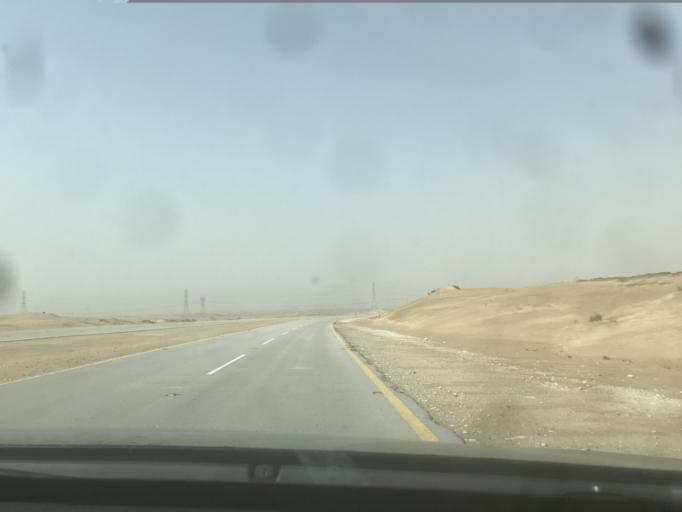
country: SA
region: Eastern Province
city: Abqaiq
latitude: 25.9253
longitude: 49.7631
